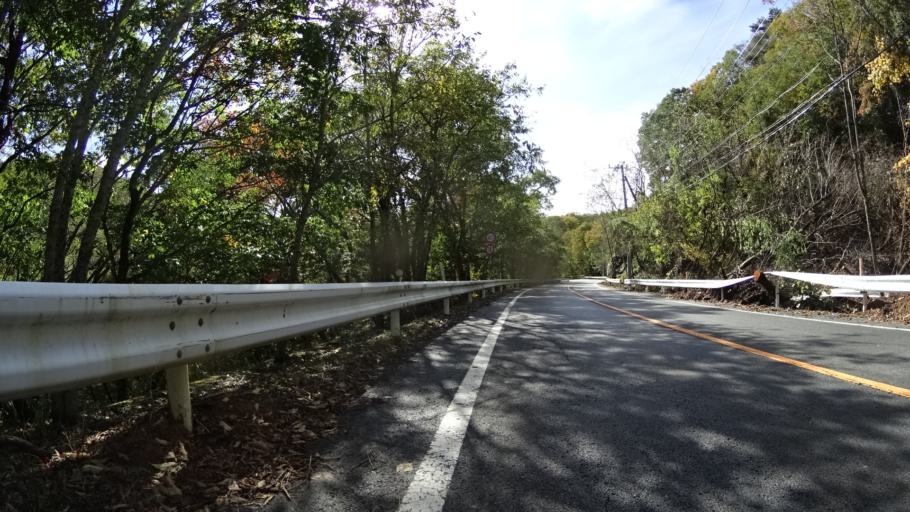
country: JP
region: Yamanashi
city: Enzan
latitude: 35.7844
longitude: 138.8010
